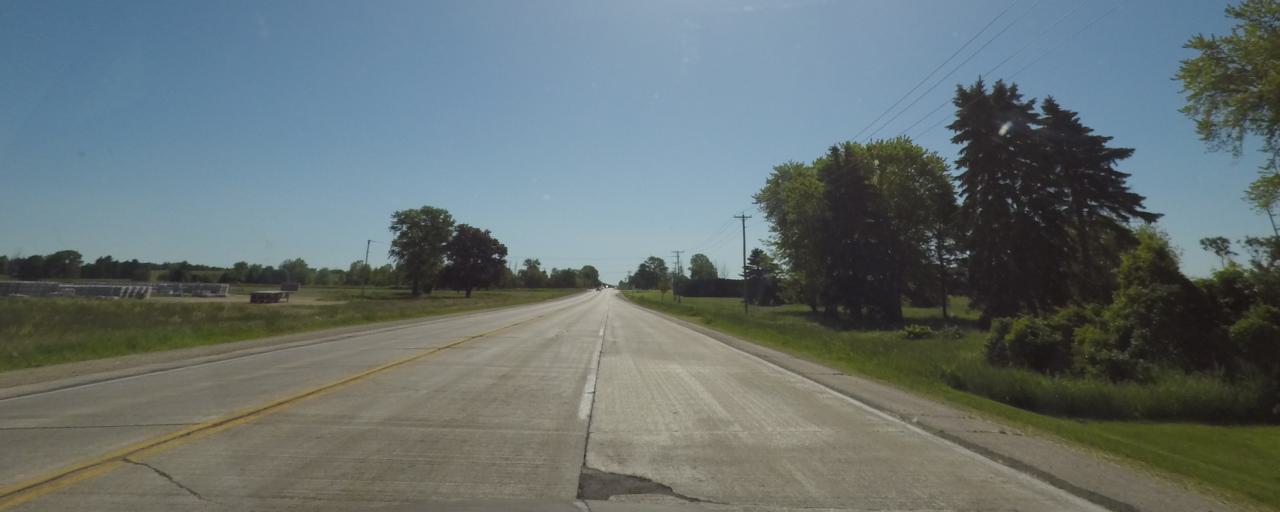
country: US
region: Wisconsin
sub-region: Fond du Lac County
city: Saint Peter
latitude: 43.7835
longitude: -88.3661
